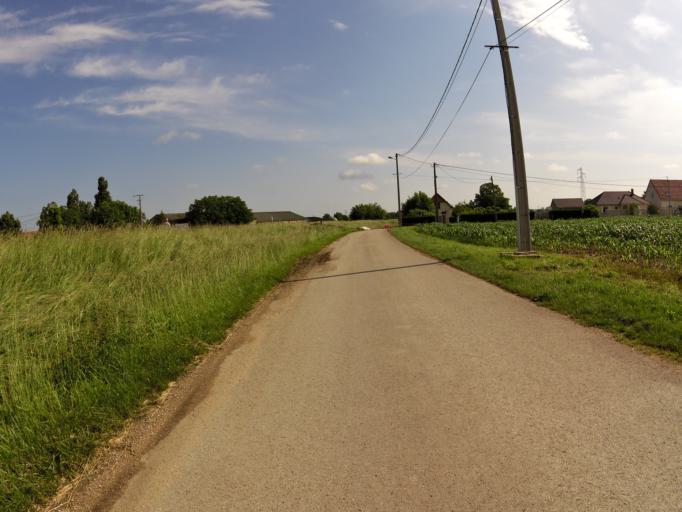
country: FR
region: Champagne-Ardenne
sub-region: Departement de l'Aube
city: Saint-Parres-aux-Tertres
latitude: 48.2687
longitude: 4.1394
